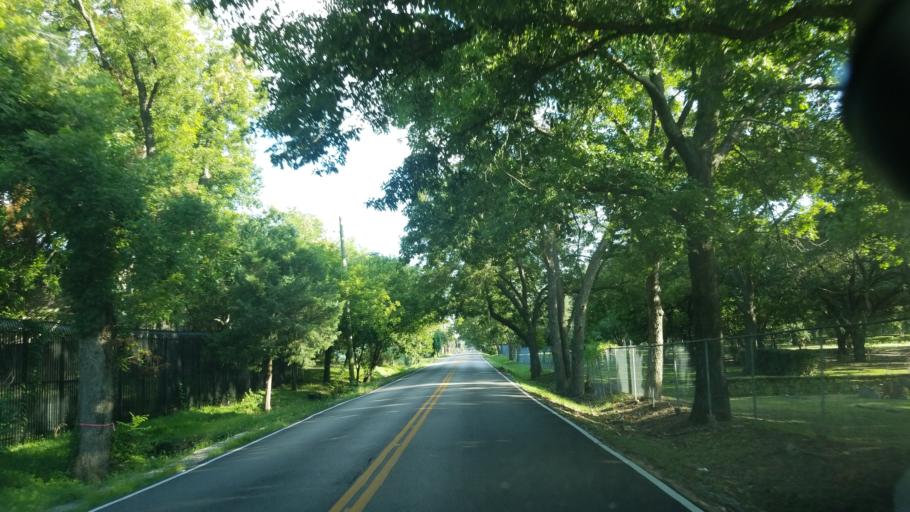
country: US
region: Texas
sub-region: Dallas County
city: Highland Park
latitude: 32.7912
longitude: -96.7172
